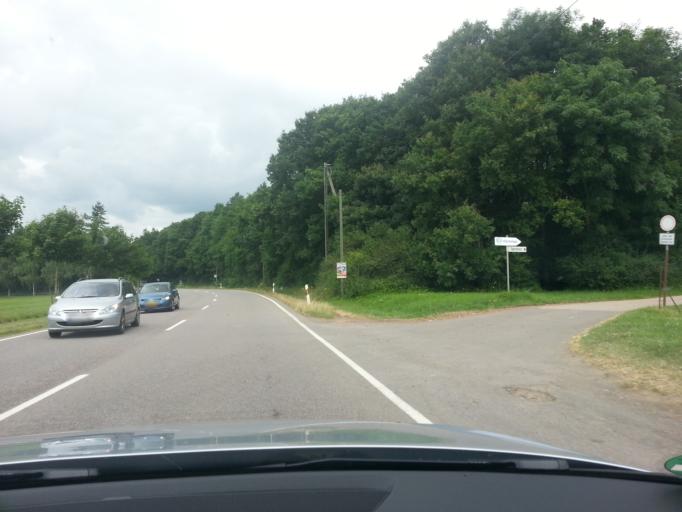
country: LU
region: Grevenmacher
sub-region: Canton de Remich
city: Remich
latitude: 49.5318
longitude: 6.4199
